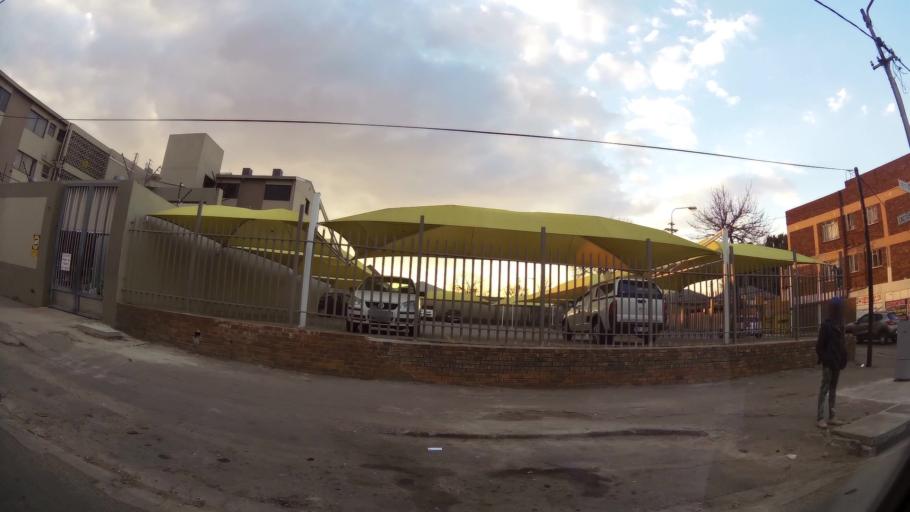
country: ZA
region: Gauteng
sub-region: Ekurhuleni Metropolitan Municipality
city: Germiston
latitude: -26.1852
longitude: 28.1702
